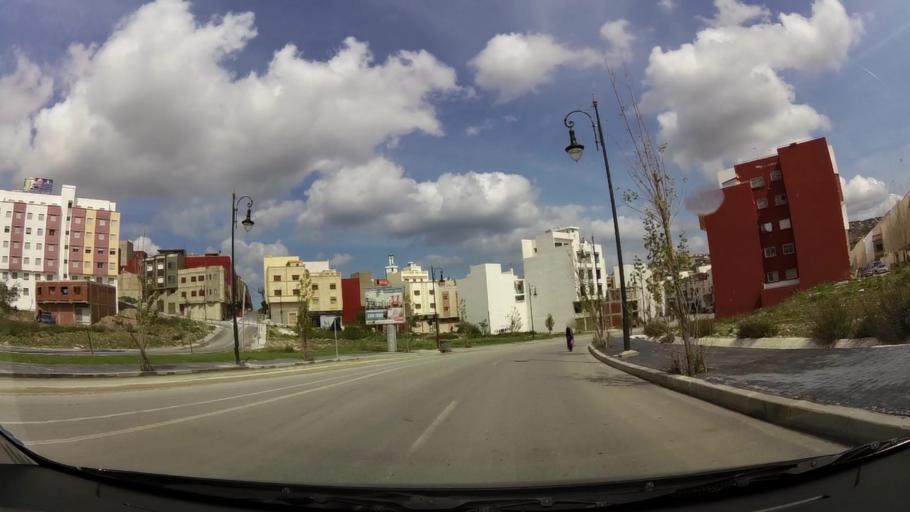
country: MA
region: Tanger-Tetouan
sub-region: Tanger-Assilah
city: Tangier
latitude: 35.7607
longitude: -5.7558
